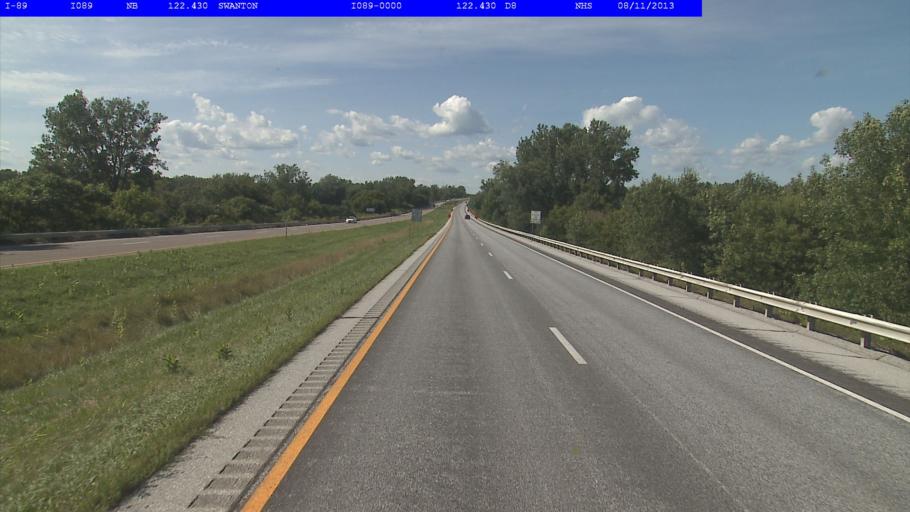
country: US
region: Vermont
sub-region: Franklin County
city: Swanton
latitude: 44.9097
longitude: -73.1000
